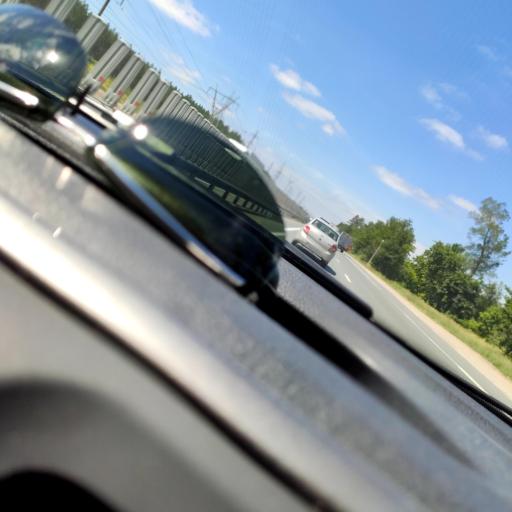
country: RU
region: Samara
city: Pribrezhnyy
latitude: 53.5142
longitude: 49.9020
